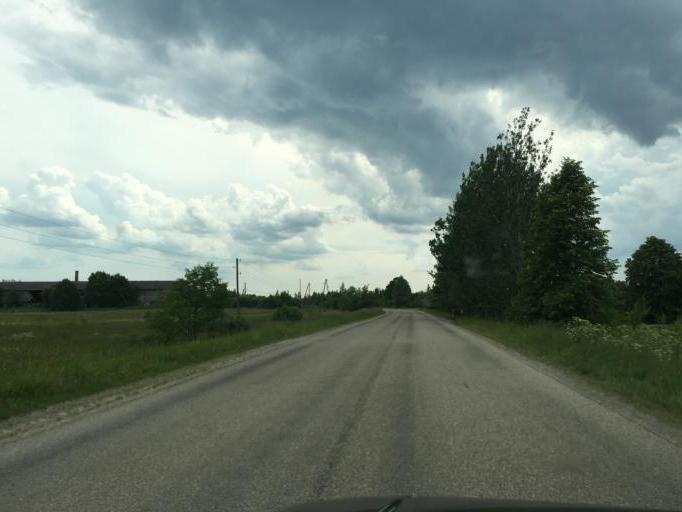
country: LV
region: Rugaju
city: Rugaji
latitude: 56.9118
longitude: 27.0666
